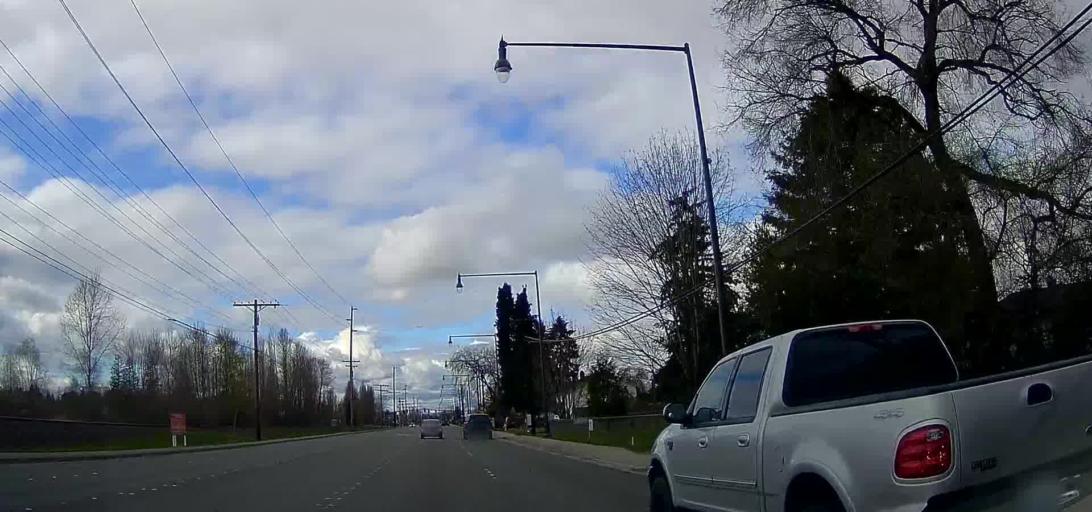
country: US
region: Washington
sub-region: Snohomish County
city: Smokey Point
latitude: 48.1086
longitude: -122.1783
